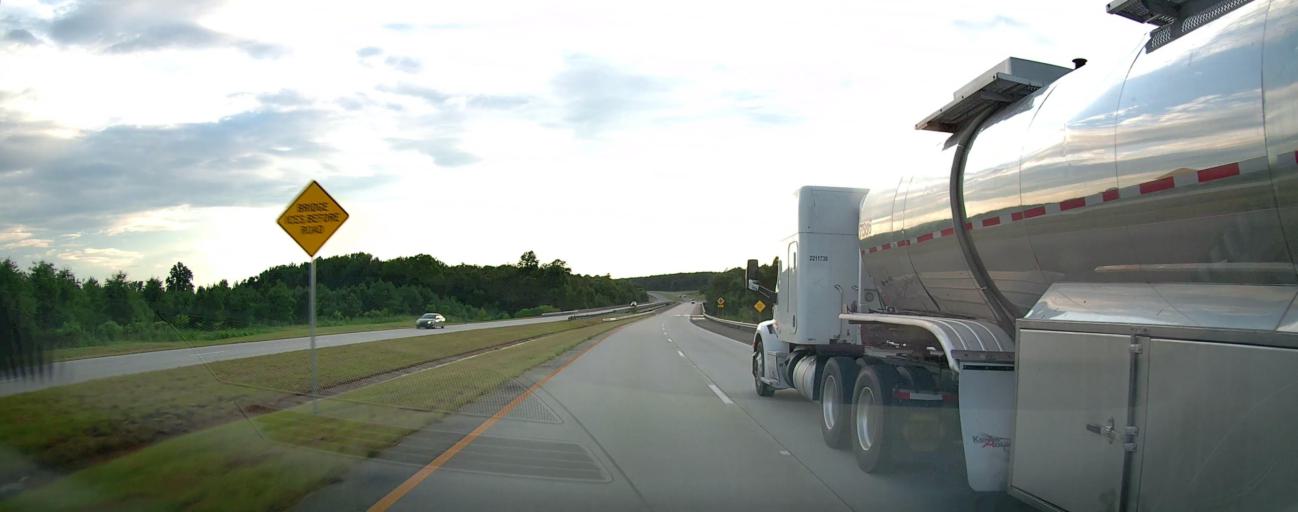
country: US
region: Georgia
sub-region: Taylor County
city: Reynolds
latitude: 32.5458
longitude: -83.9955
